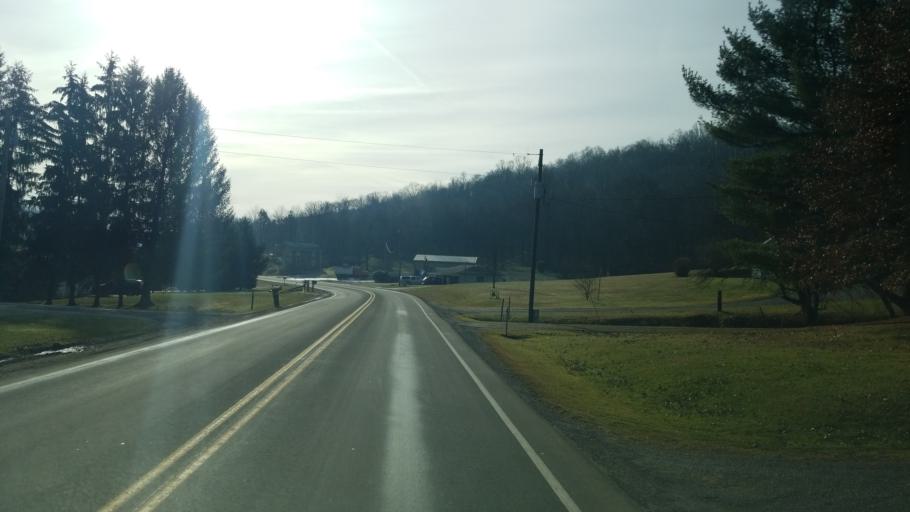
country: US
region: Pennsylvania
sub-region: Indiana County
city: Chevy Chase Heights
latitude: 40.7751
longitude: -79.1542
